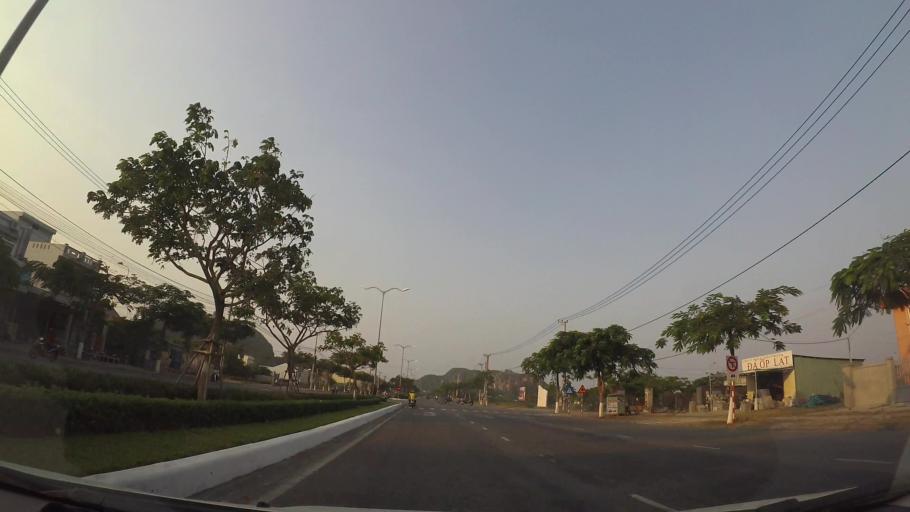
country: VN
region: Da Nang
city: Ngu Hanh Son
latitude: 15.9931
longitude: 108.2583
